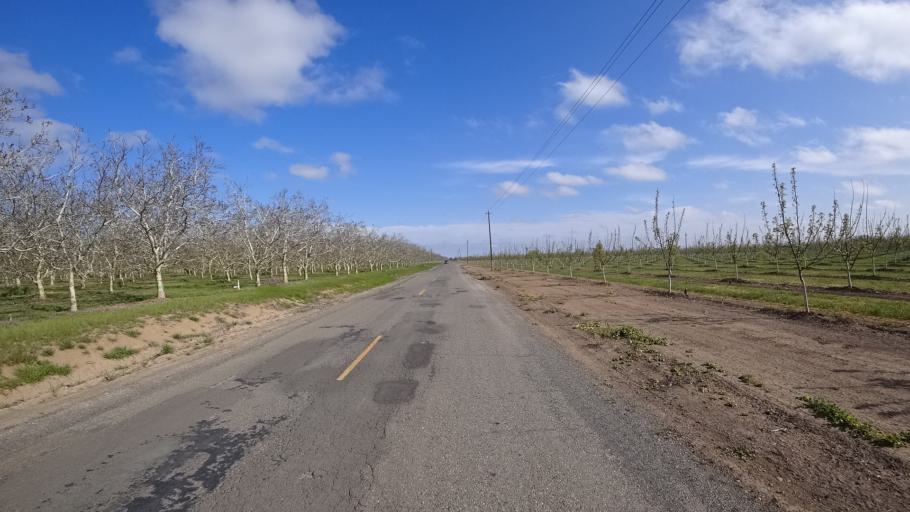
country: US
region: California
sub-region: Glenn County
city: Willows
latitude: 39.4756
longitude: -121.9678
